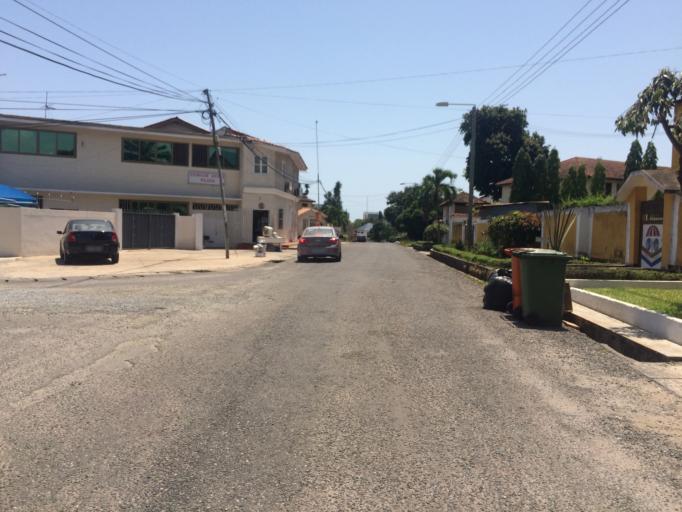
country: GH
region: Greater Accra
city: Accra
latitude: 5.5674
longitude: -0.1881
